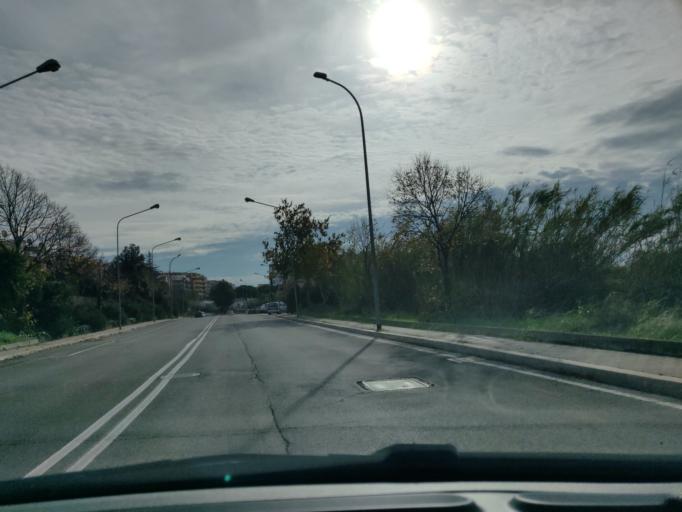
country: IT
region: Latium
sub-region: Citta metropolitana di Roma Capitale
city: Civitavecchia
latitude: 42.1005
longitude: 11.8090
